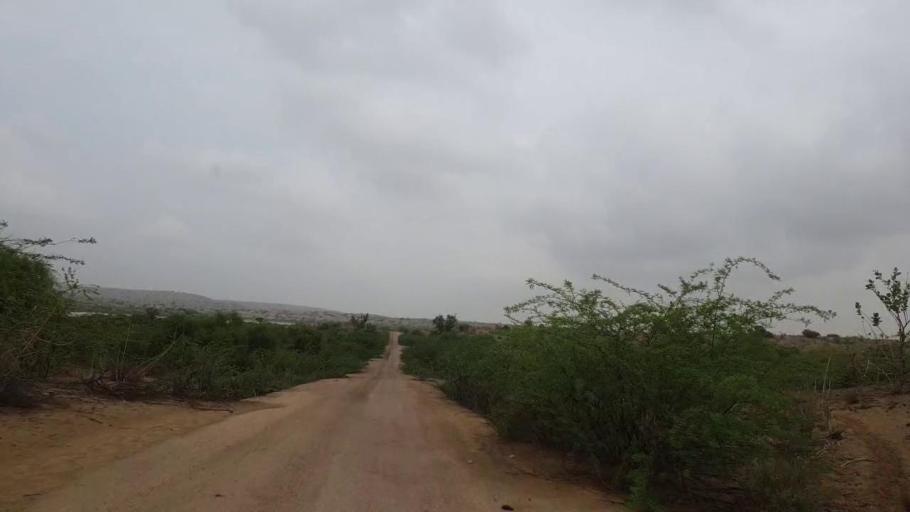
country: PK
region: Sindh
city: Diplo
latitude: 24.5185
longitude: 69.4709
